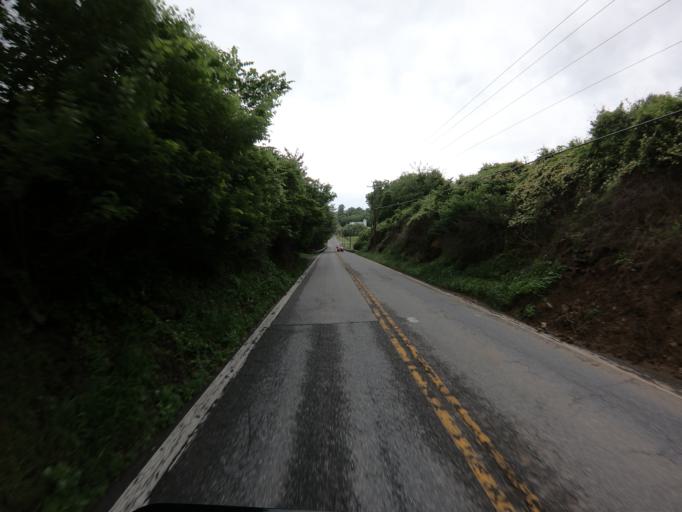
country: US
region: Maryland
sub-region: Frederick County
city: Middletown
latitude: 39.4518
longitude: -77.5655
